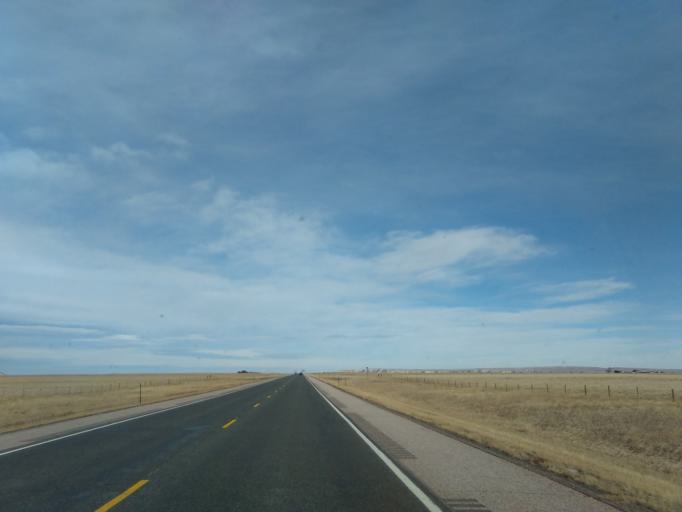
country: US
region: Wyoming
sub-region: Laramie County
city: Pine Bluffs
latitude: 41.6027
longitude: -104.2602
